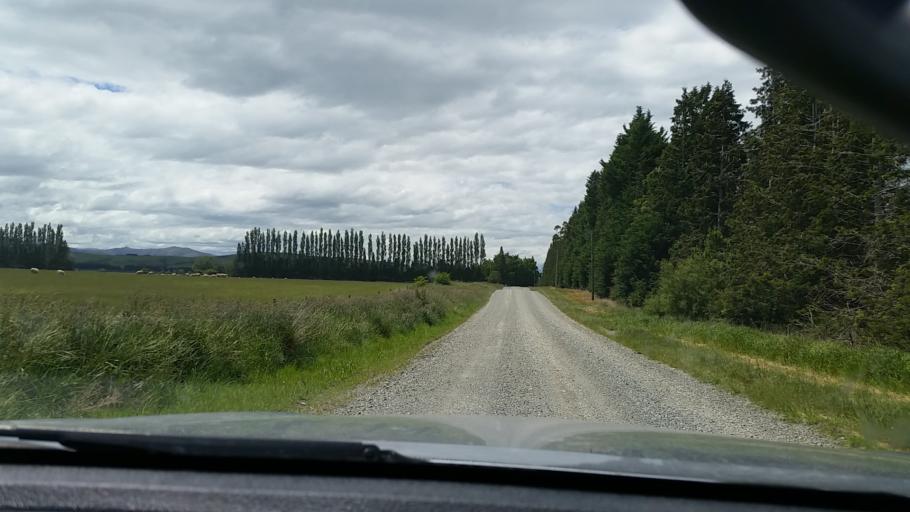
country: NZ
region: Southland
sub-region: Southland District
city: Winton
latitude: -45.7741
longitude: 168.5820
